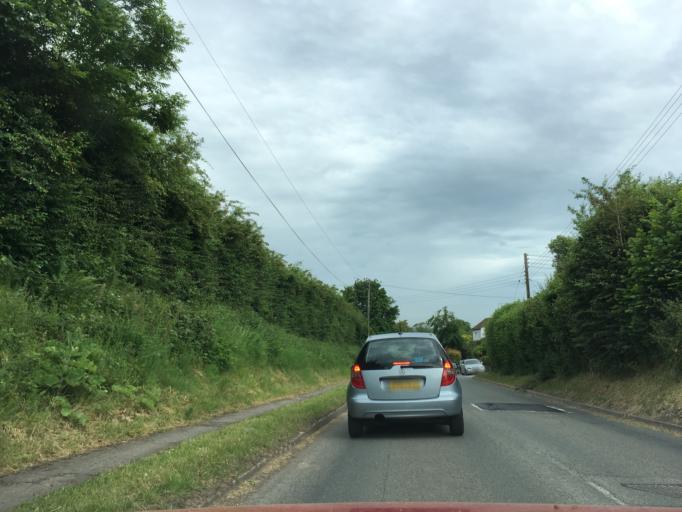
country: GB
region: England
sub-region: North Somerset
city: Portishead
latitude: 51.4639
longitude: -2.7581
